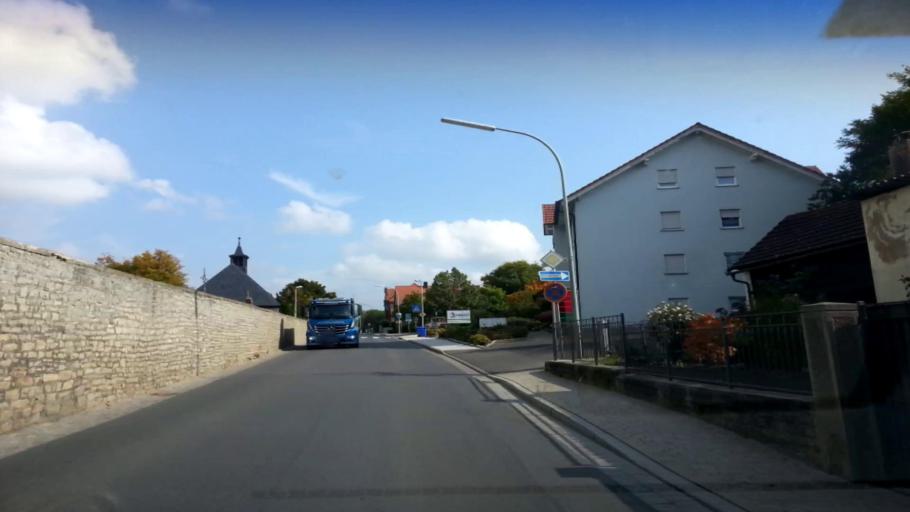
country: DE
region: Bavaria
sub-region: Regierungsbezirk Unterfranken
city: Wiesentheid
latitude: 49.7958
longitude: 10.3465
